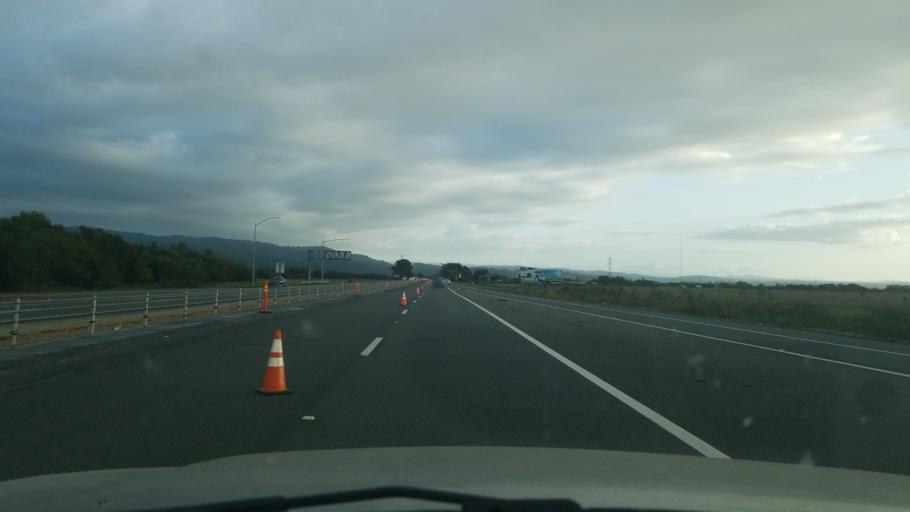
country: US
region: California
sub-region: Humboldt County
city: Arcata
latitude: 40.8595
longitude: -124.0829
